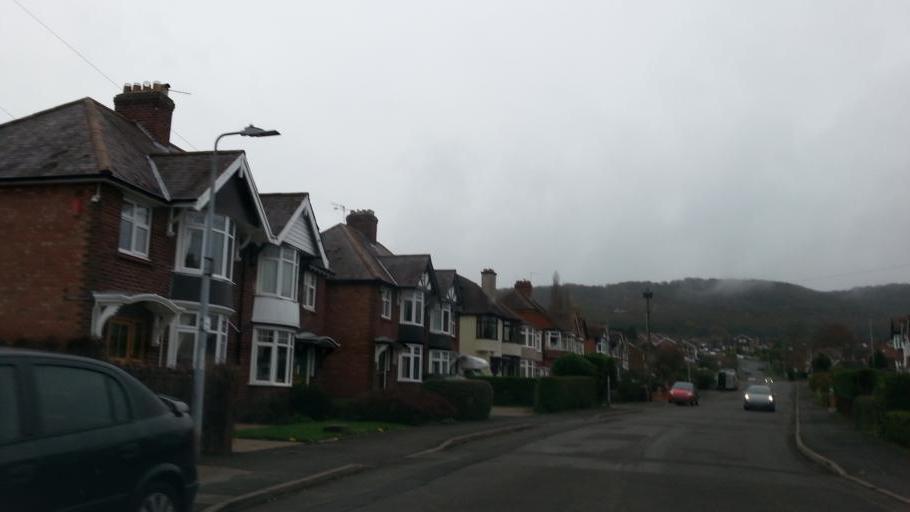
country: GB
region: England
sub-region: Telford and Wrekin
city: Wellington
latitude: 52.6944
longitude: -2.5276
